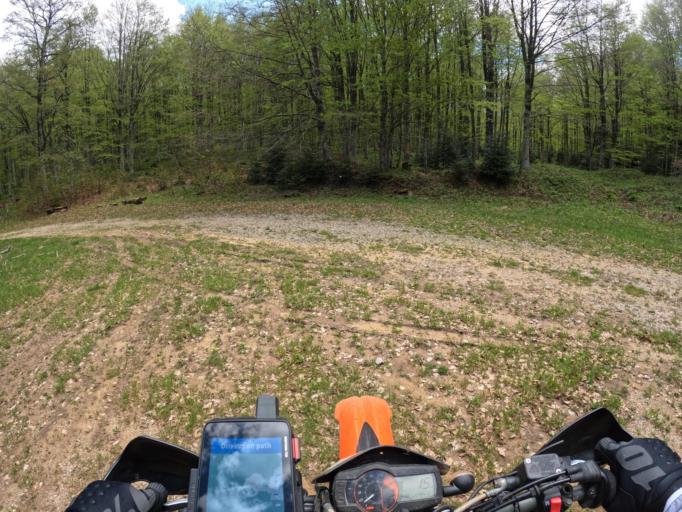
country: HR
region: Zadarska
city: Gracac
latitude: 44.4831
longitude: 15.8526
